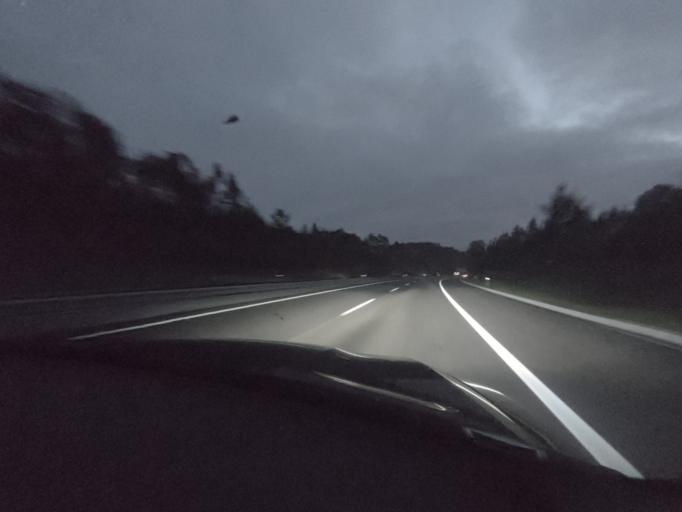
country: PT
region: Leiria
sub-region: Leiria
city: Caranguejeira
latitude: 39.7819
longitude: -8.7377
